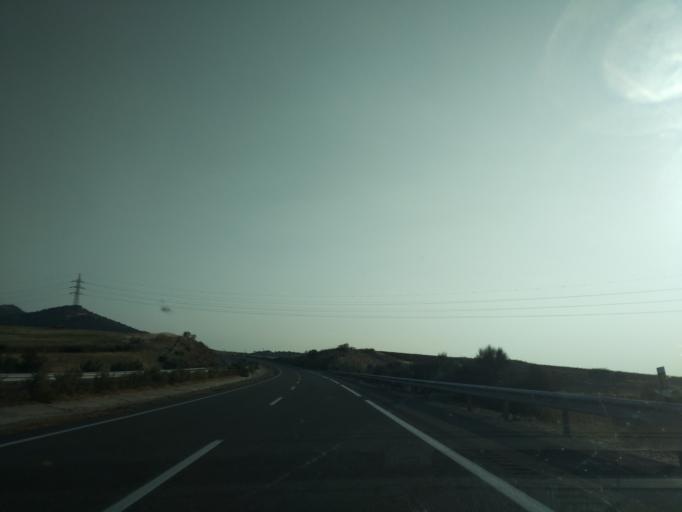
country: ES
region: Castille and Leon
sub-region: Provincia de Avila
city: Ojos-Albos
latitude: 40.7470
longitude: -4.4846
